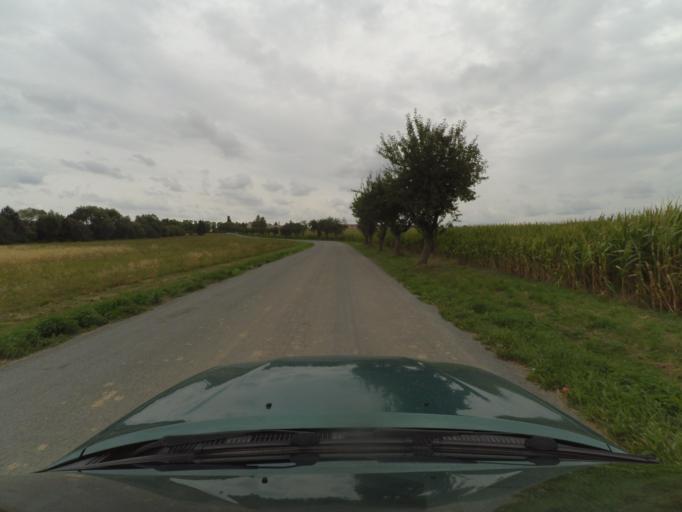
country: CZ
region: Plzensky
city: Kozlany
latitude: 49.9661
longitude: 13.5376
